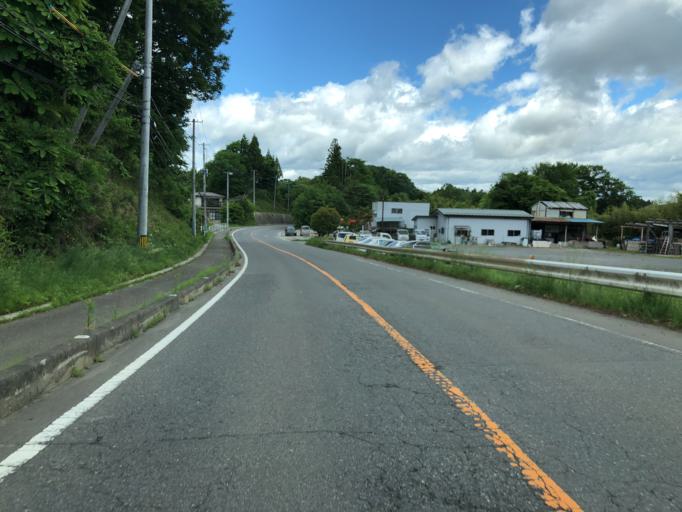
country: JP
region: Fukushima
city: Nihommatsu
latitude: 37.5750
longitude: 140.4562
